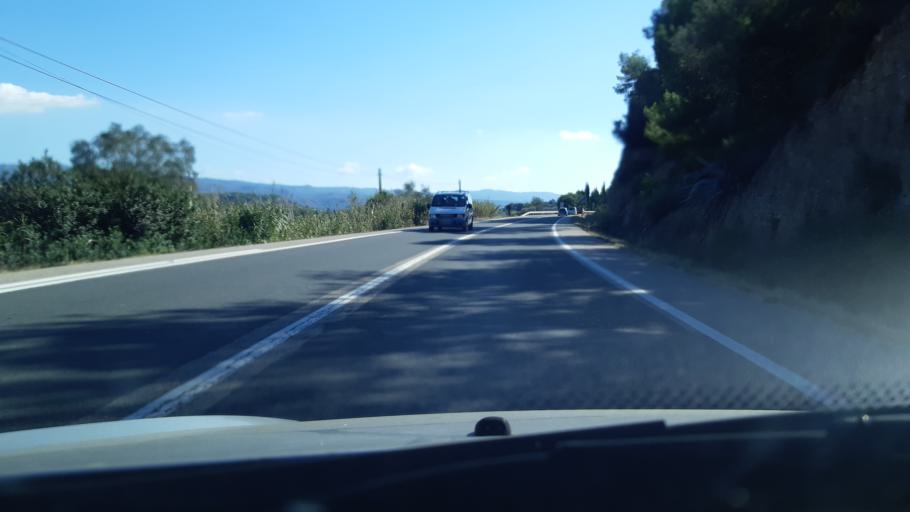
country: ES
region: Catalonia
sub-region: Provincia de Tarragona
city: Tivenys
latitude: 40.8969
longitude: 0.4875
